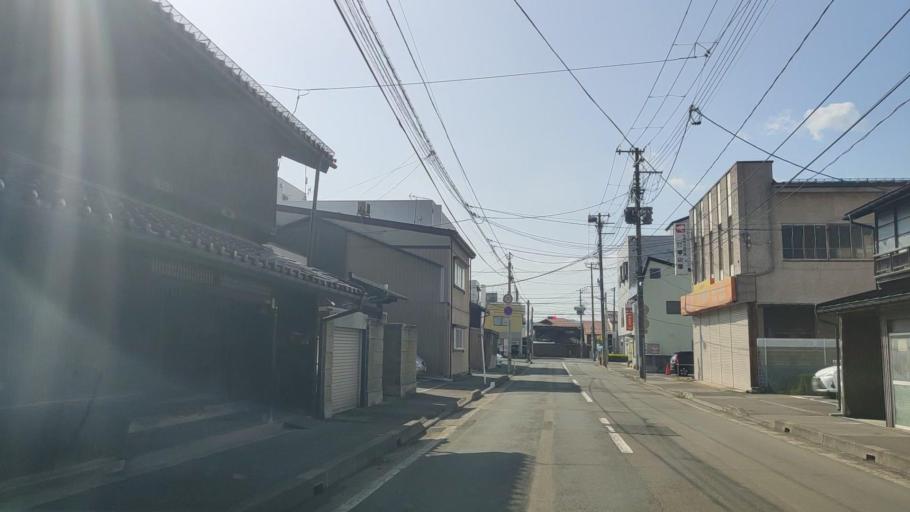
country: JP
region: Iwate
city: Morioka-shi
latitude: 39.6954
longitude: 141.1542
